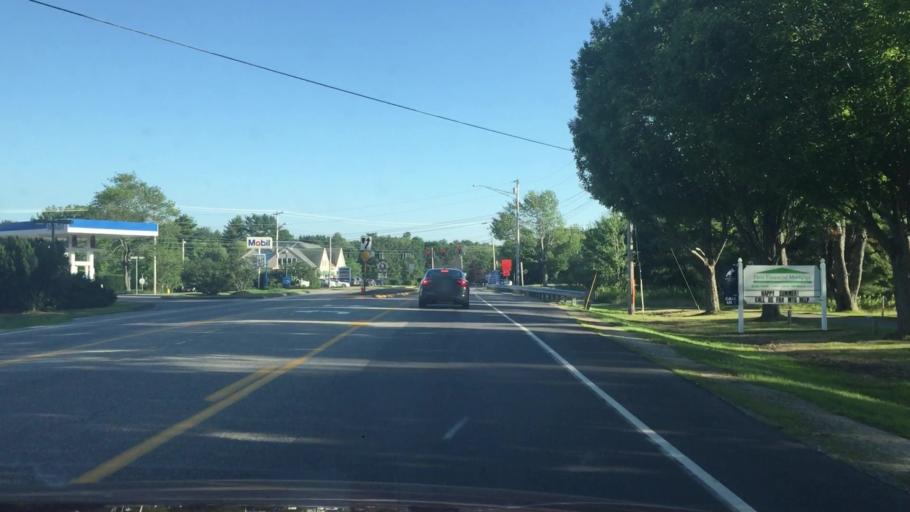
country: US
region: Maine
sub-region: Cumberland County
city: Yarmouth
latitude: 43.7940
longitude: -70.1886
